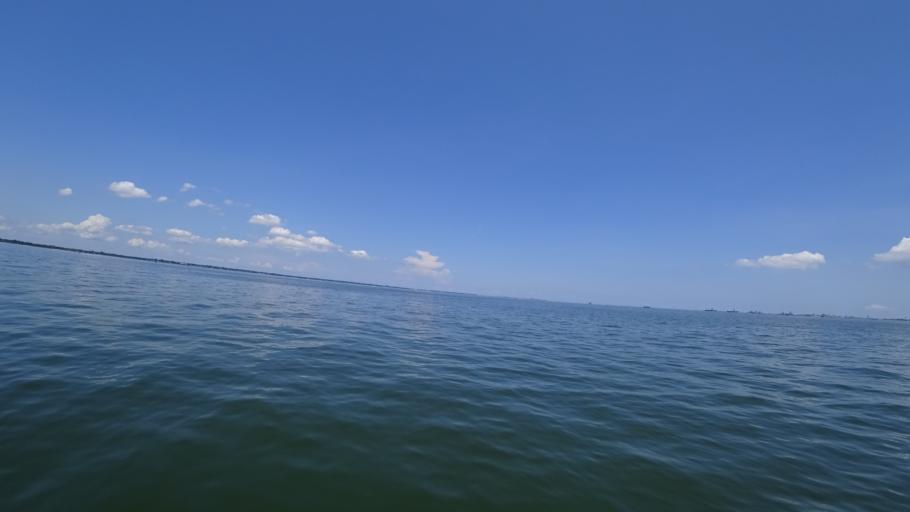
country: US
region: Virginia
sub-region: City of Newport News
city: Newport News
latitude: 36.9475
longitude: -76.3904
